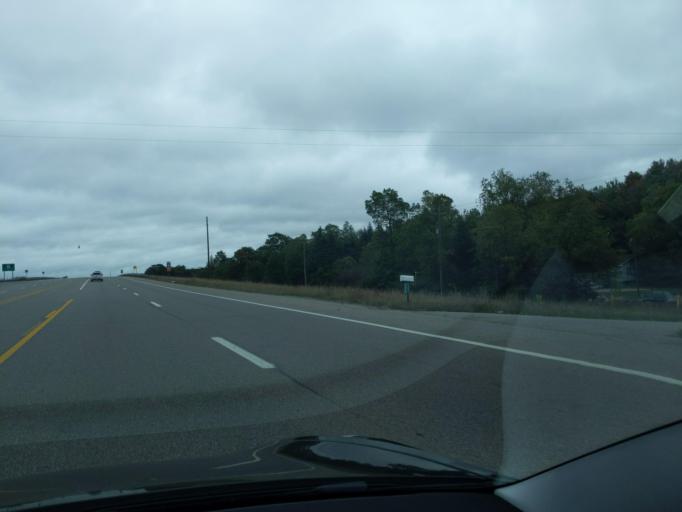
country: US
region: Michigan
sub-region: Wexford County
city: Cadillac
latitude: 44.2813
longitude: -85.3931
